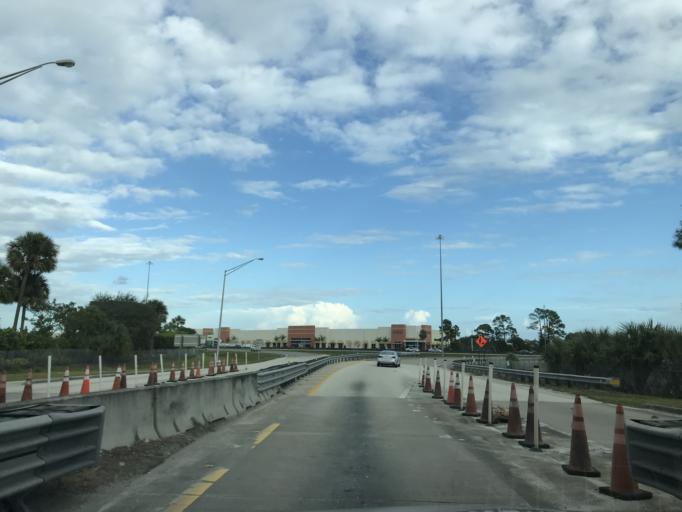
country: US
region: Florida
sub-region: Palm Beach County
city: Lake Belvedere Estates
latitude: 26.6853
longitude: -80.1645
